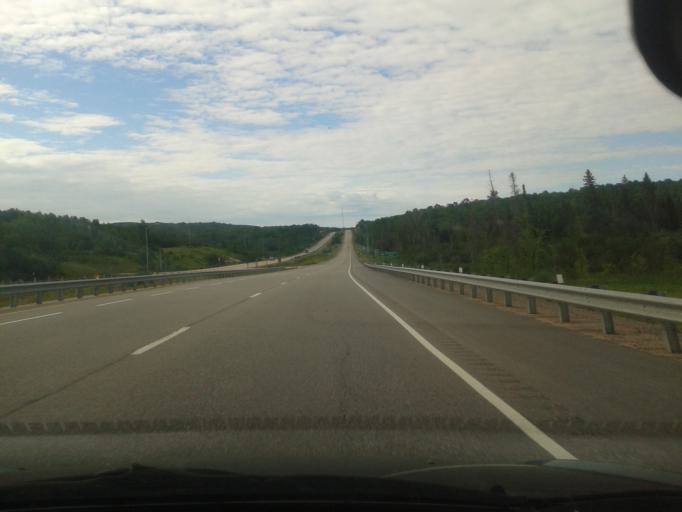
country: CA
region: Ontario
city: Powassan
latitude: 46.0438
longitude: -79.3419
